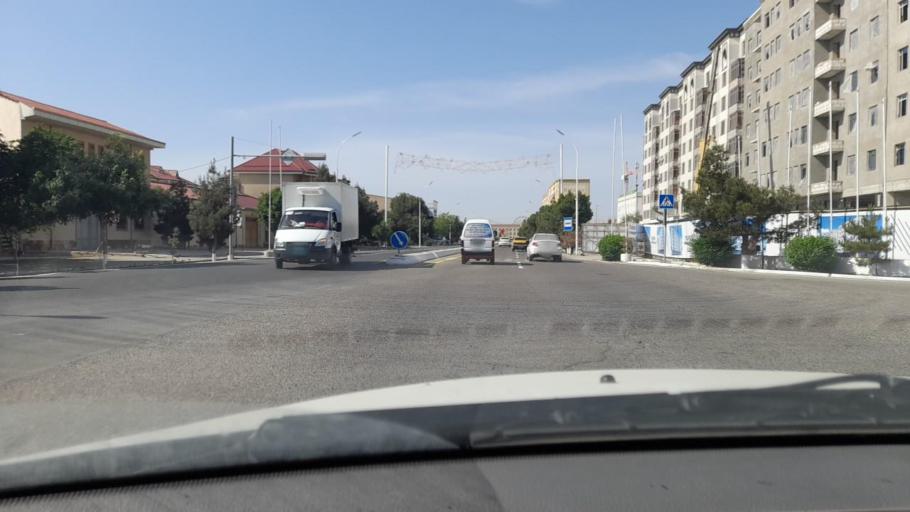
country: UZ
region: Bukhara
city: Bukhara
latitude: 39.7886
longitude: 64.4322
